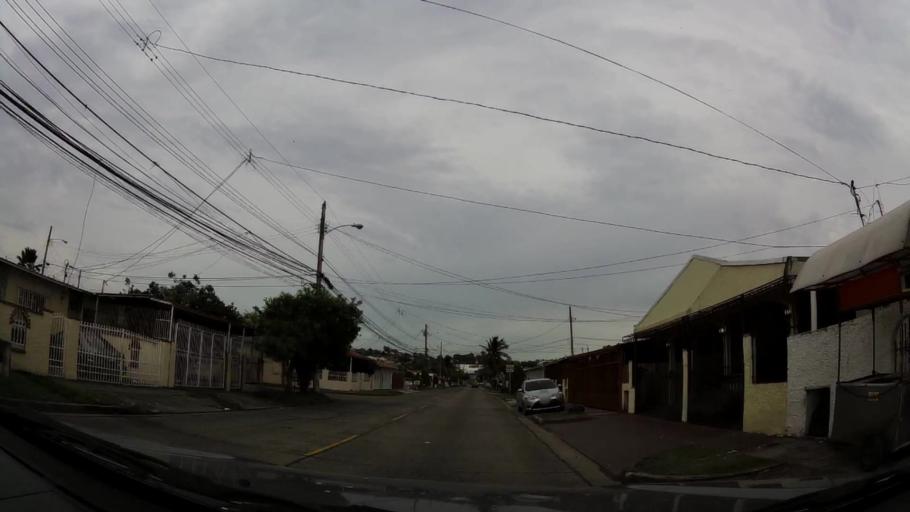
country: PA
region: Panama
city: San Miguelito
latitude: 9.0370
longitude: -79.4766
